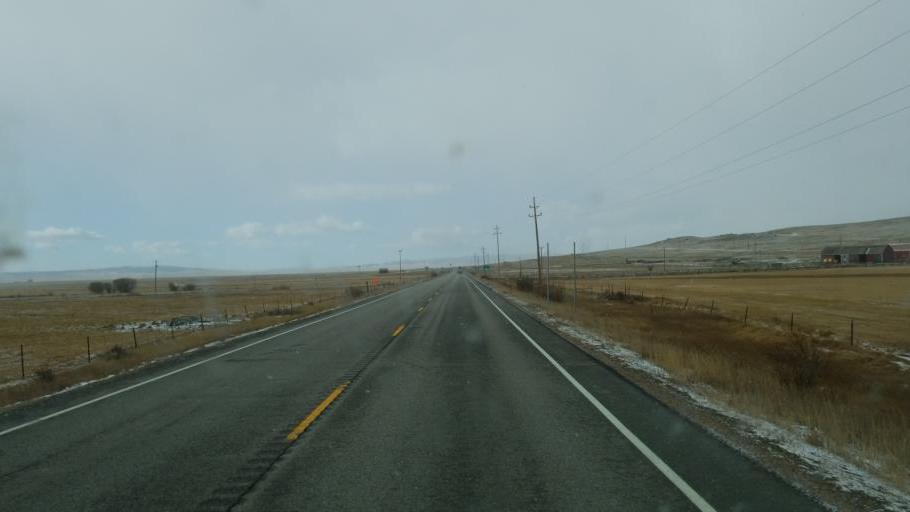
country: US
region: Colorado
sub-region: Summit County
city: Breckenridge
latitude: 39.3933
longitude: -105.7859
